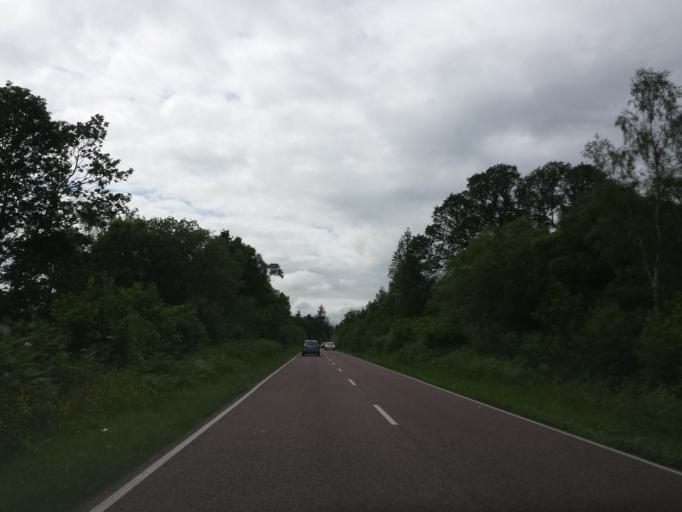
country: GB
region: Scotland
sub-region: Highland
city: Fort William
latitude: 56.8555
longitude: -5.2179
